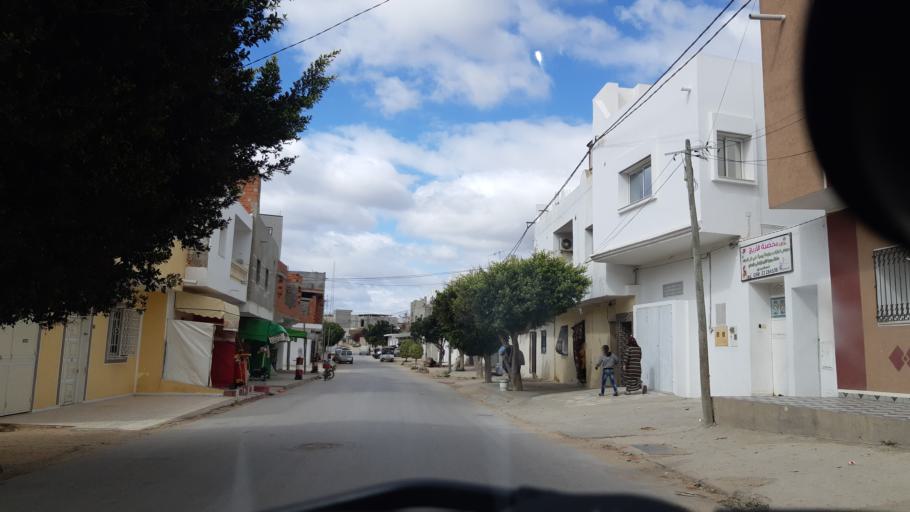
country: TN
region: Susah
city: Akouda
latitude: 35.8678
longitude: 10.5242
